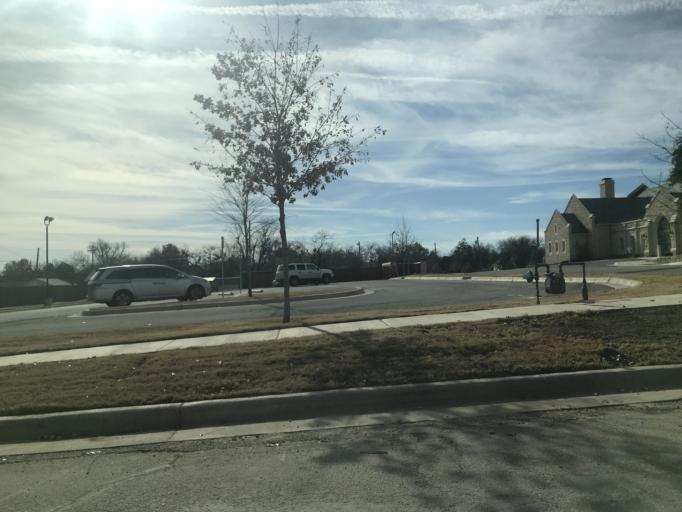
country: US
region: Texas
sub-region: Taylor County
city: Abilene
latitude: 32.4443
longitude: -99.7448
